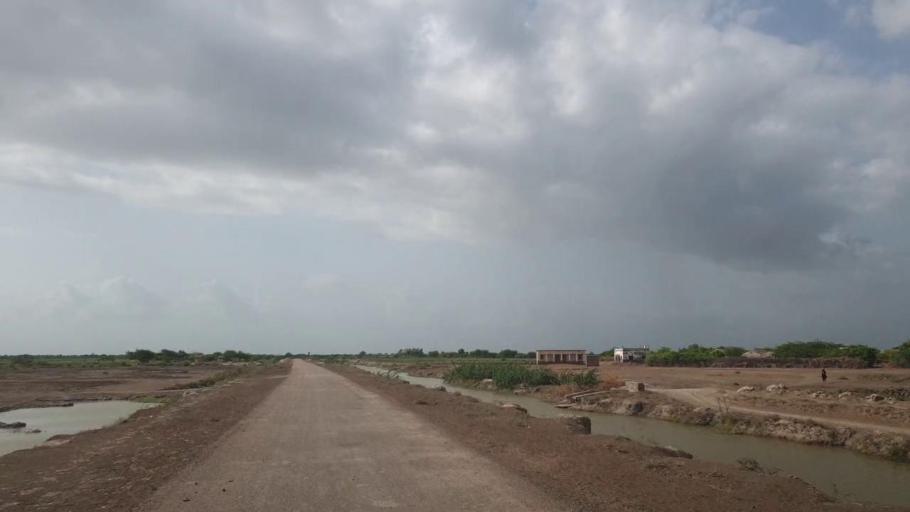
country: PK
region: Sindh
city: Kadhan
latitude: 24.5685
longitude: 69.0625
